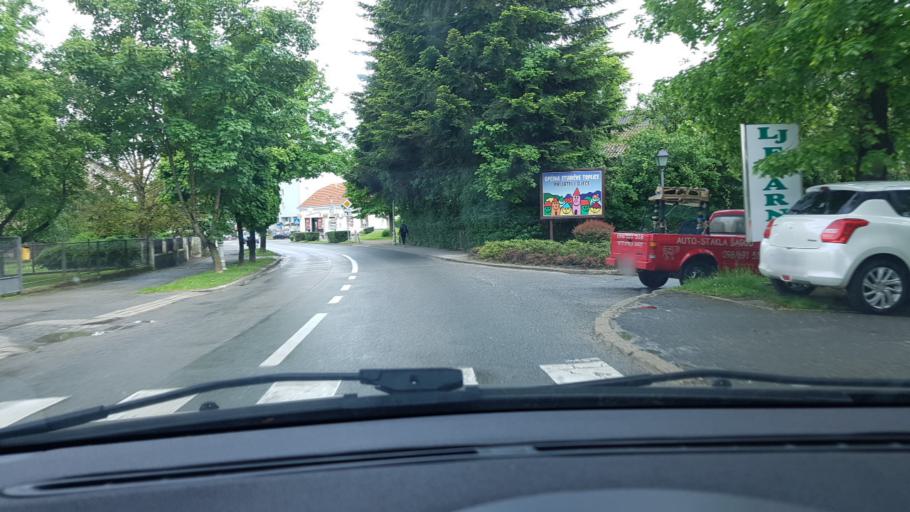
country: HR
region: Krapinsko-Zagorska
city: Oroslavje
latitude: 45.9779
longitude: 15.9303
